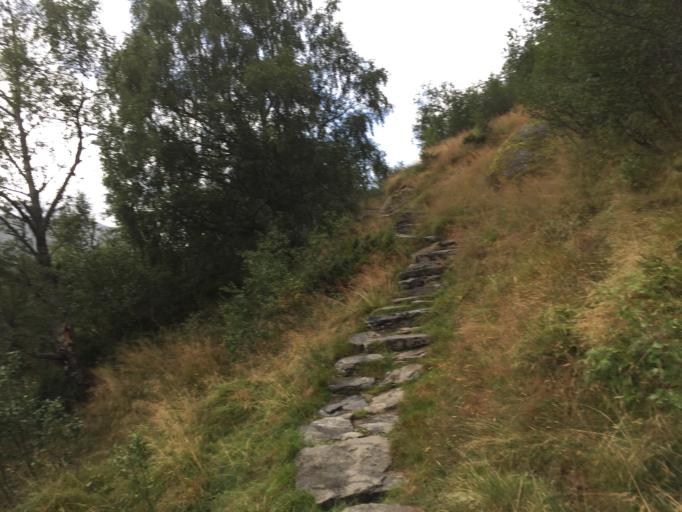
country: NO
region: More og Romsdal
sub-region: Norddal
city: Valldal
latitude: 62.1017
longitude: 7.2226
